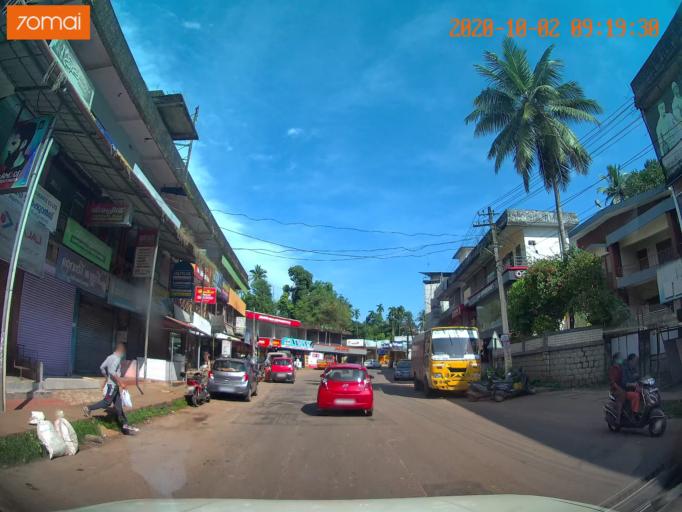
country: IN
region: Kerala
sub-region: Kozhikode
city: Naduvannur
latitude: 11.5631
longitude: 75.7569
